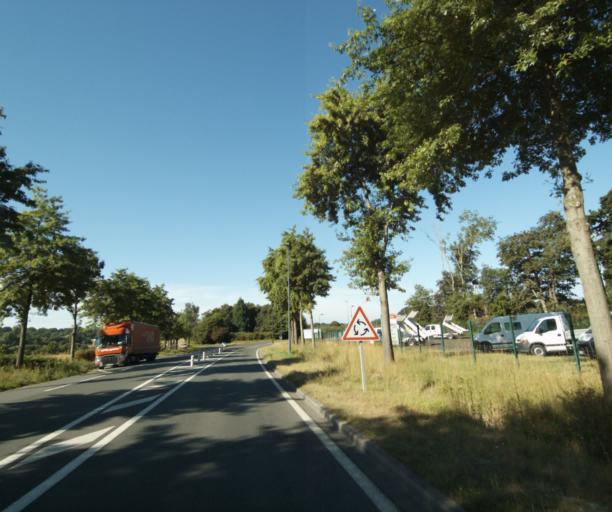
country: FR
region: Pays de la Loire
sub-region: Departement de la Mayenne
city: Laval
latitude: 48.0510
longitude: -0.7336
